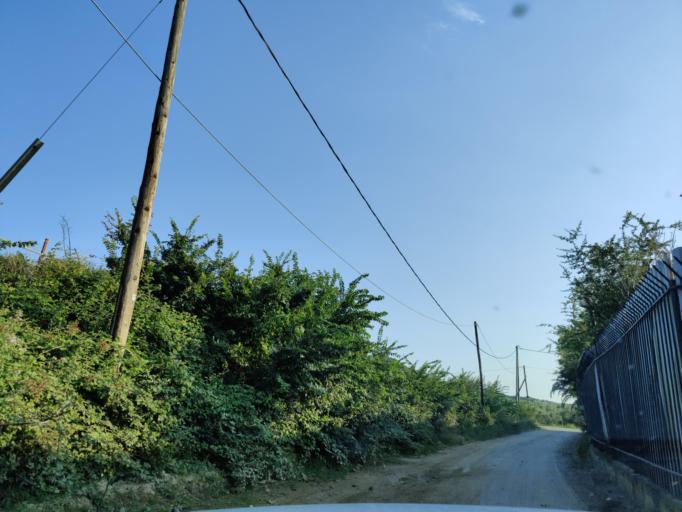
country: GR
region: East Macedonia and Thrace
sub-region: Nomos Kavalas
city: Nea Peramos
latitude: 40.8286
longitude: 24.2960
